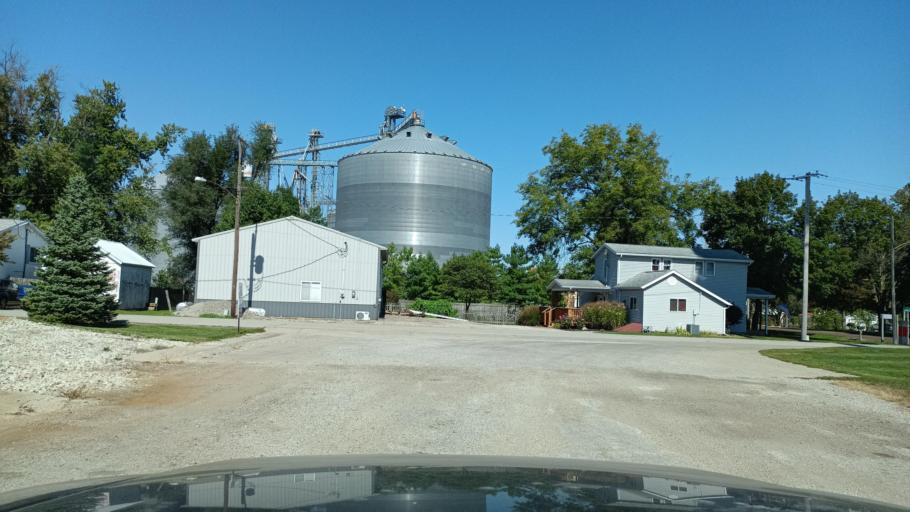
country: US
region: Illinois
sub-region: McLean County
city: Danvers
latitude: 40.6133
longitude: -89.2049
